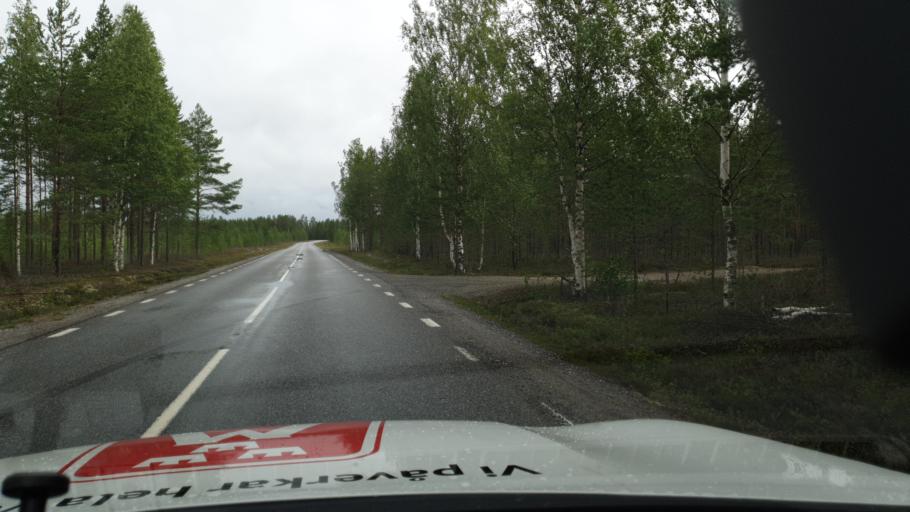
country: SE
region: Vaesterbotten
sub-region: Umea Kommun
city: Saevar
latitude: 63.9770
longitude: 20.5056
